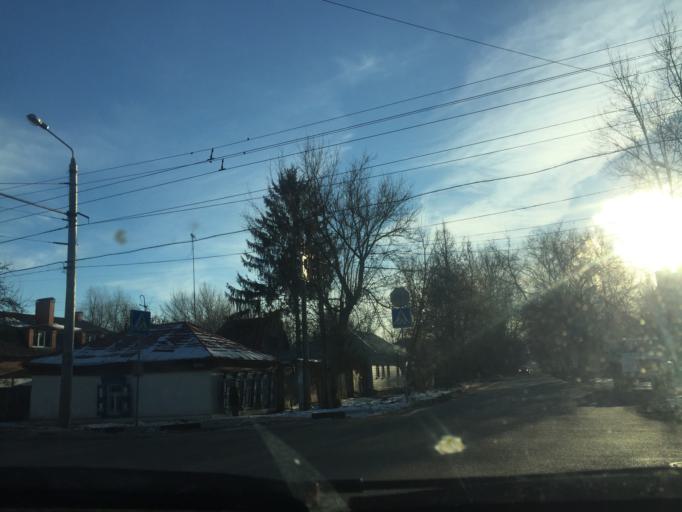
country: RU
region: Tula
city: Tula
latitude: 54.2096
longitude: 37.5957
